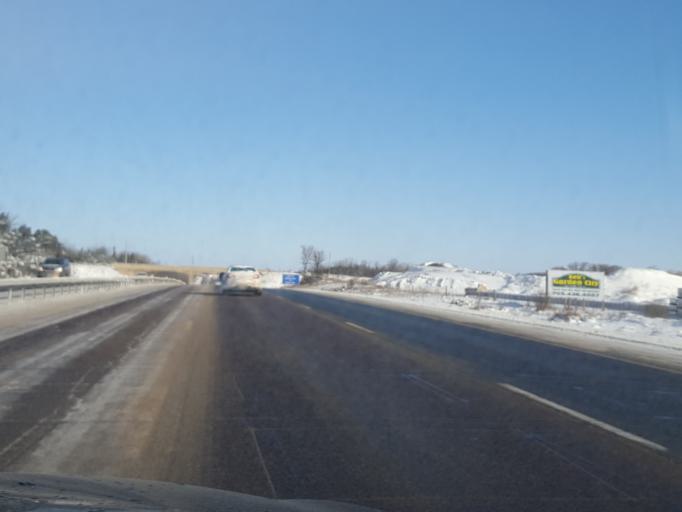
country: CA
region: Ontario
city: Innisfil
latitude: 44.3072
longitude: -79.6837
